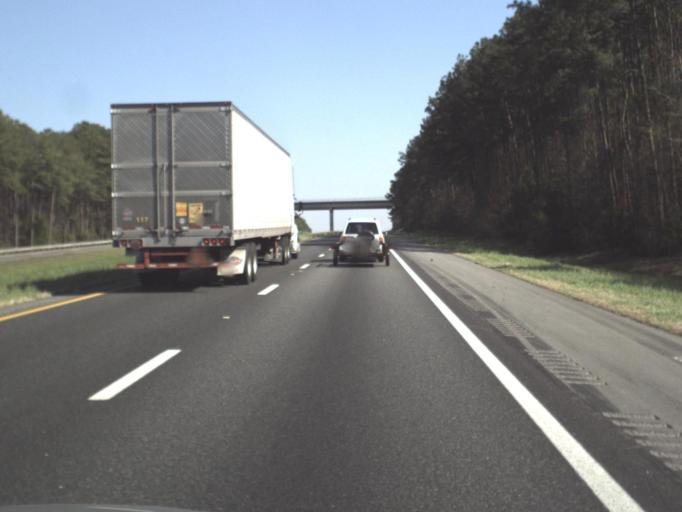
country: US
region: Florida
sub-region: Gadsden County
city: Chattahoochee
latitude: 30.6252
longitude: -84.8500
